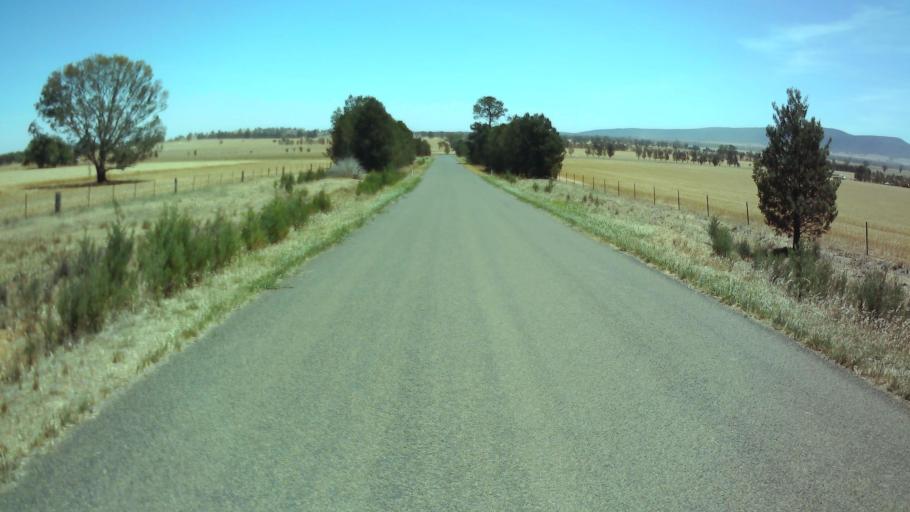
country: AU
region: New South Wales
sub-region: Weddin
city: Grenfell
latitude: -34.0496
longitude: 148.1788
